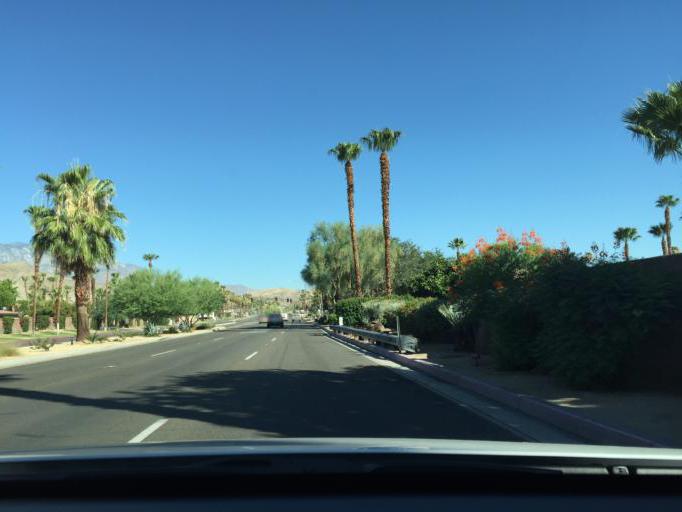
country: US
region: California
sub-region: Riverside County
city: Rancho Mirage
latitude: 33.7567
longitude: -116.4340
